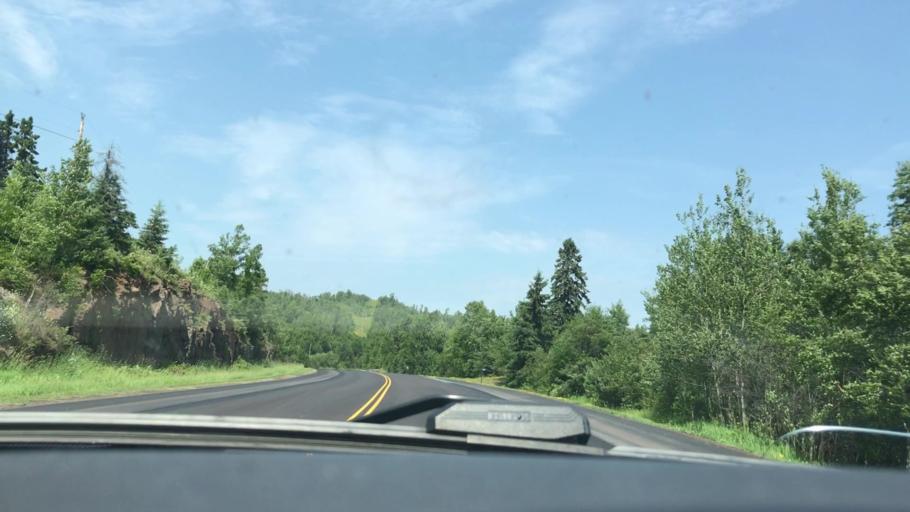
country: US
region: Minnesota
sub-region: Lake County
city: Silver Bay
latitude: 47.3626
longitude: -91.1739
